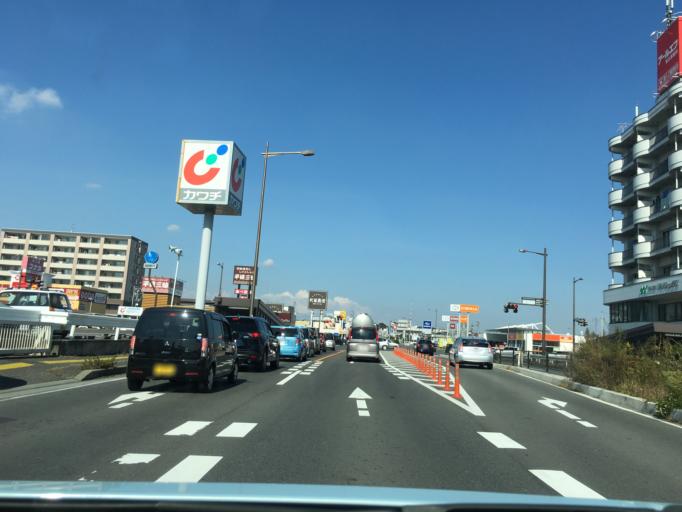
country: JP
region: Fukushima
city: Sukagawa
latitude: 37.2984
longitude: 140.3676
